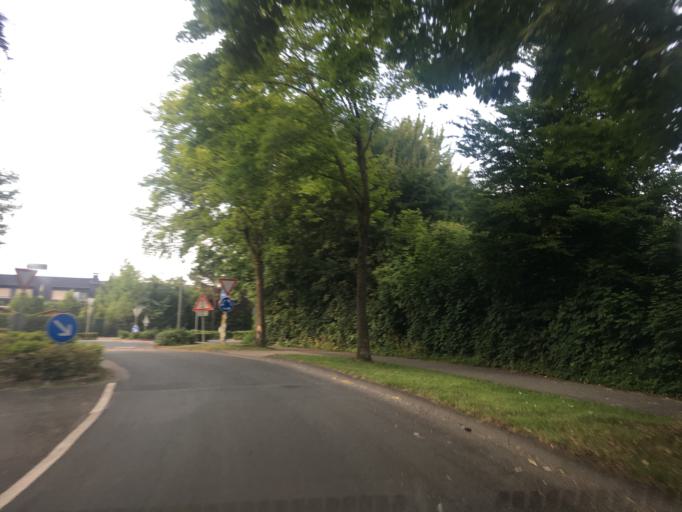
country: DE
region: North Rhine-Westphalia
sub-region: Regierungsbezirk Munster
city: Senden
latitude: 51.8539
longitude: 7.4750
